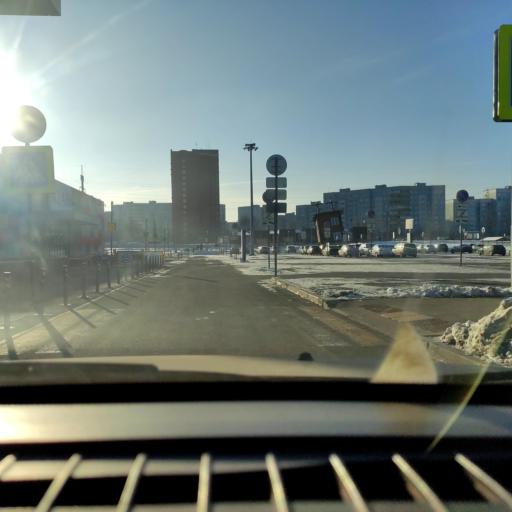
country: RU
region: Samara
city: Tol'yatti
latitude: 53.5501
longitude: 49.3453
